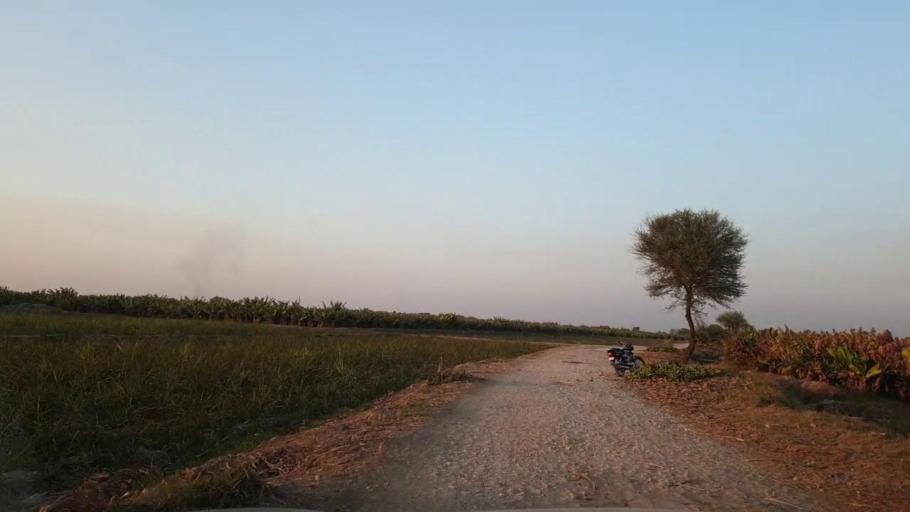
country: PK
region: Sindh
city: Berani
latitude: 25.6644
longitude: 68.7707
